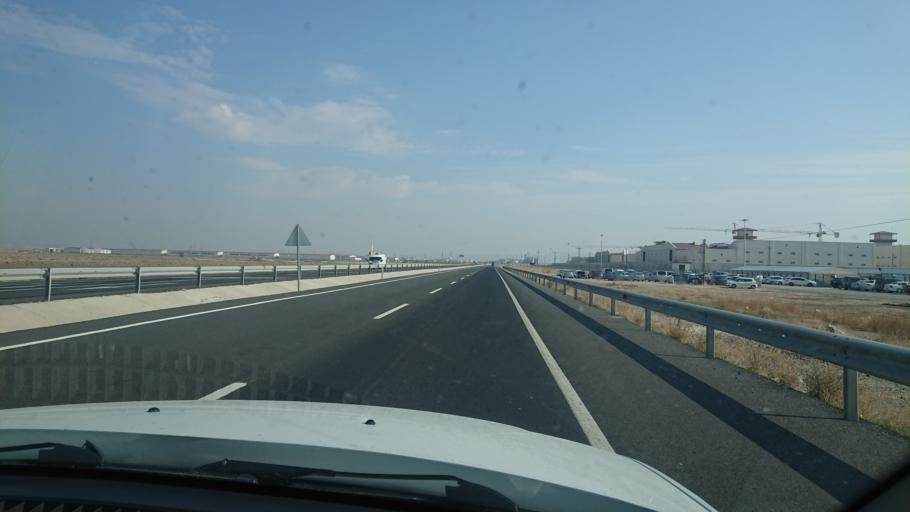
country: TR
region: Aksaray
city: Aksaray
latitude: 38.3345
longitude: 33.9235
